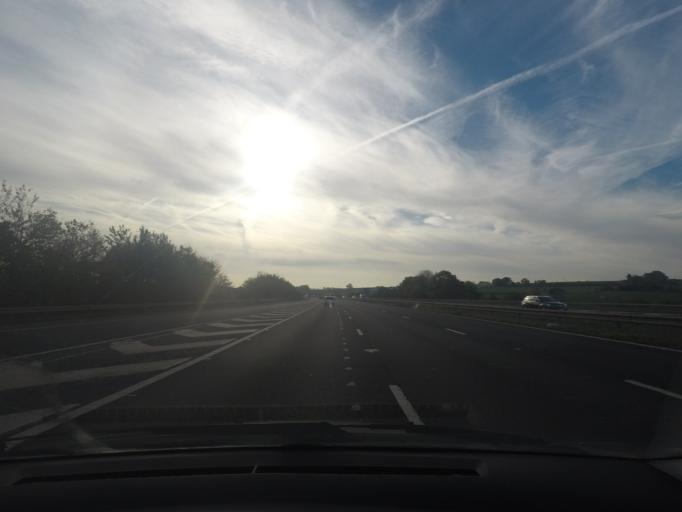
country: GB
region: England
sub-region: Barnsley
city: Darton
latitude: 53.6002
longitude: -1.5488
